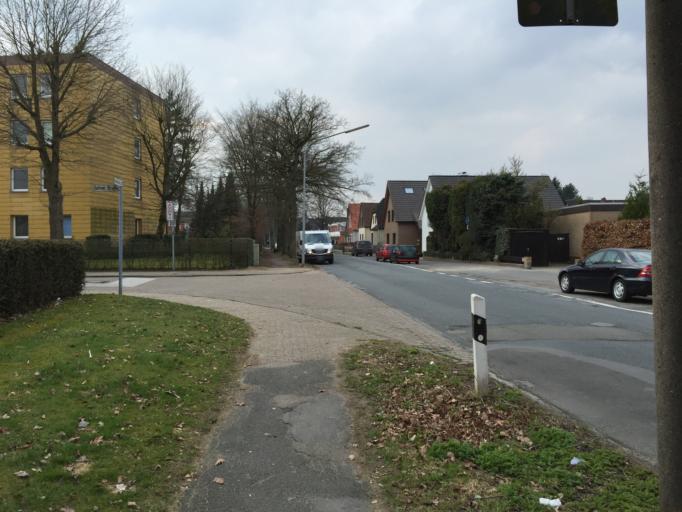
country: DE
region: Lower Saxony
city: Oldenburg
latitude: 53.1666
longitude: 8.2403
